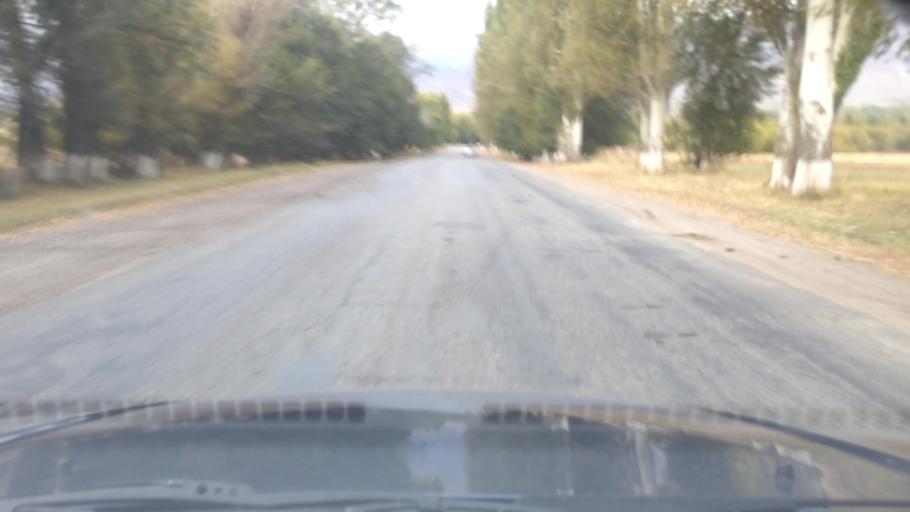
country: KG
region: Ysyk-Koel
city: Tyup
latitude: 42.7857
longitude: 78.2689
